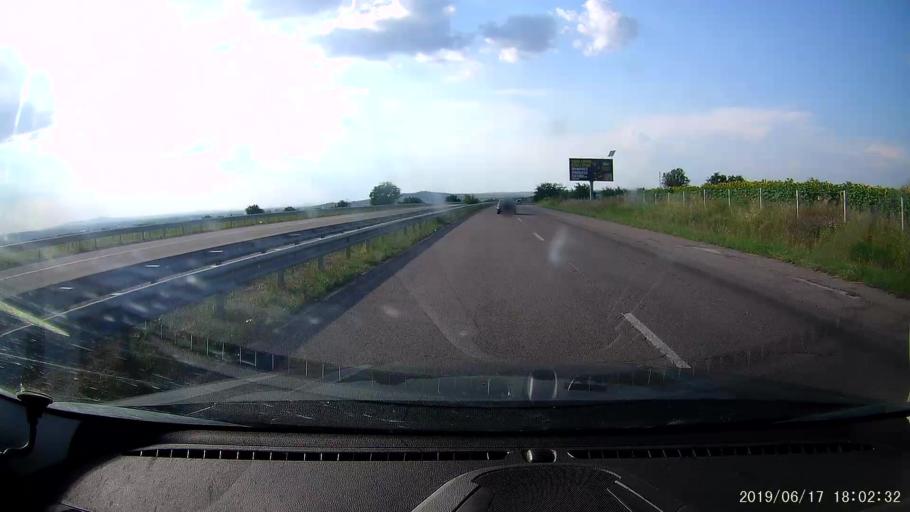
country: BG
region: Khaskovo
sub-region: Obshtina Svilengrad
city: Svilengrad
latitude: 41.7614
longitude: 26.2293
